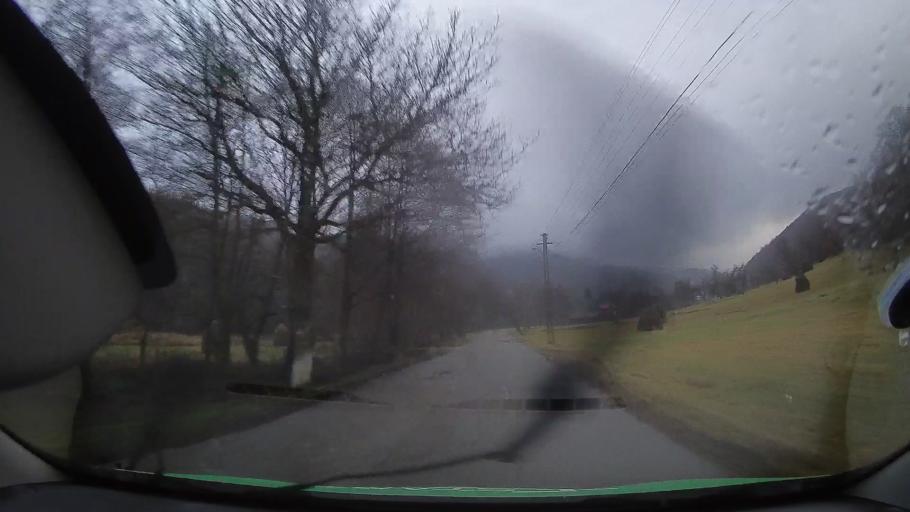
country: RO
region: Hunedoara
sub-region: Comuna Ribita
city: Ribita
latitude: 46.2547
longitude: 22.7483
